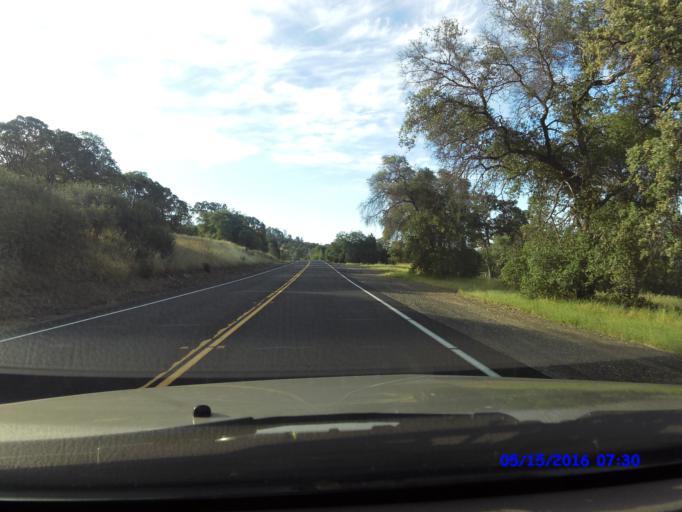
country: US
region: California
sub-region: Tuolumne County
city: Tuolumne City
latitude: 37.7258
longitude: -120.2066
